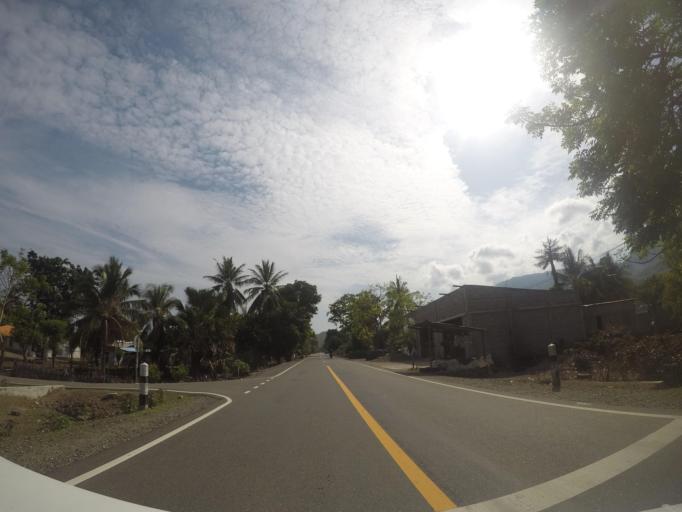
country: ID
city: Metinaro
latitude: -8.4962
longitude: 125.8230
